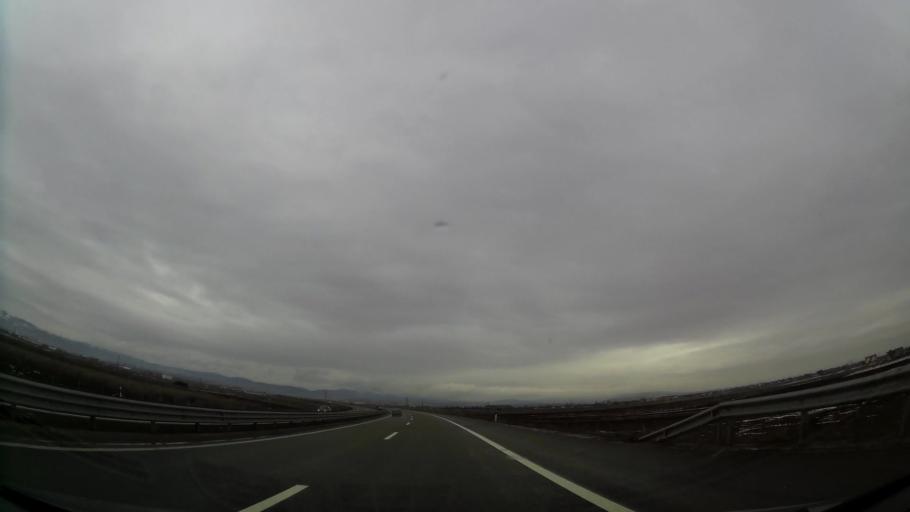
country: XK
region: Pristina
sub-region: Lipjan
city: Lipljan
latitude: 42.5312
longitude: 21.1426
